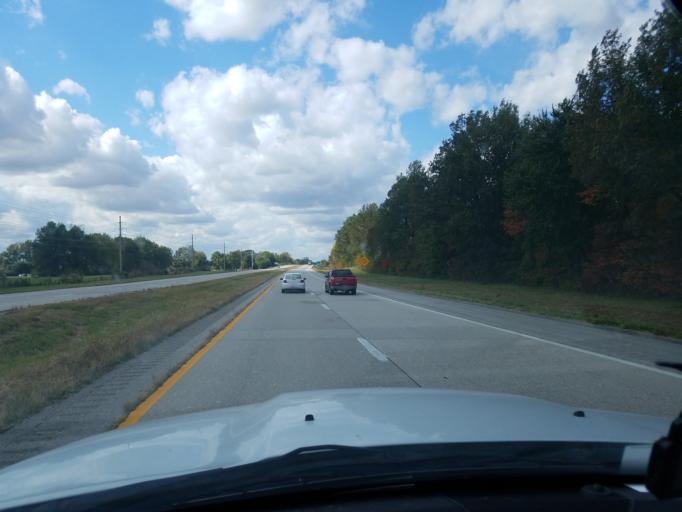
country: US
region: Kentucky
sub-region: Daviess County
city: Owensboro
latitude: 37.7656
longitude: -87.1686
